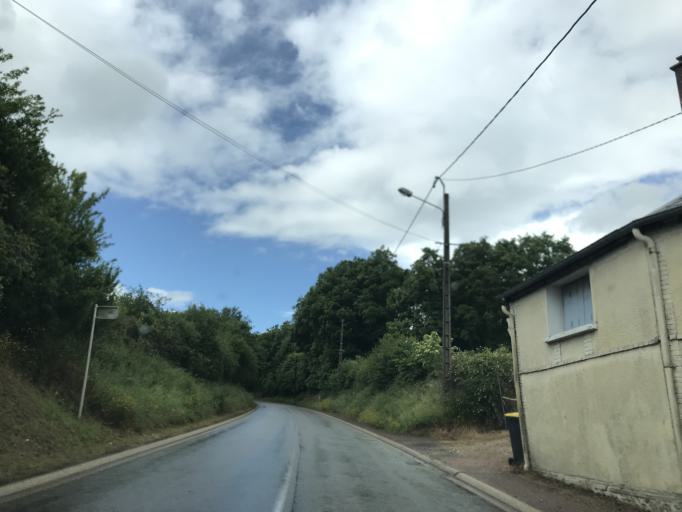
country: FR
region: Haute-Normandie
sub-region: Departement de l'Eure
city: Damville
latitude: 48.8717
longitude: 1.0682
